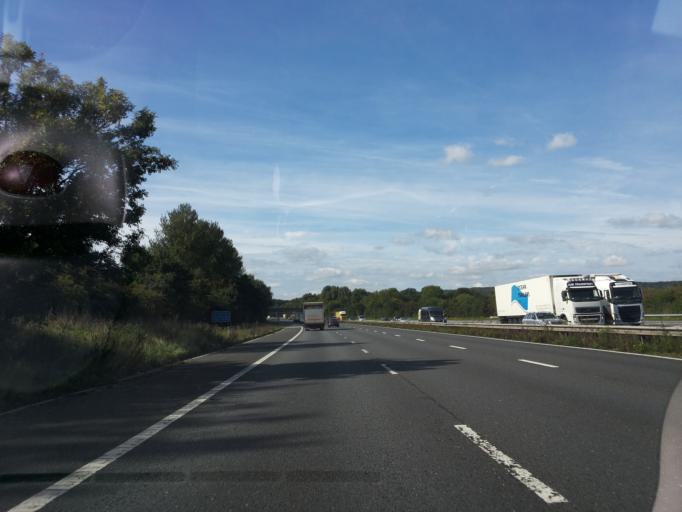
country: GB
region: England
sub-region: Kent
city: Larkfield
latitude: 51.3099
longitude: 0.4223
